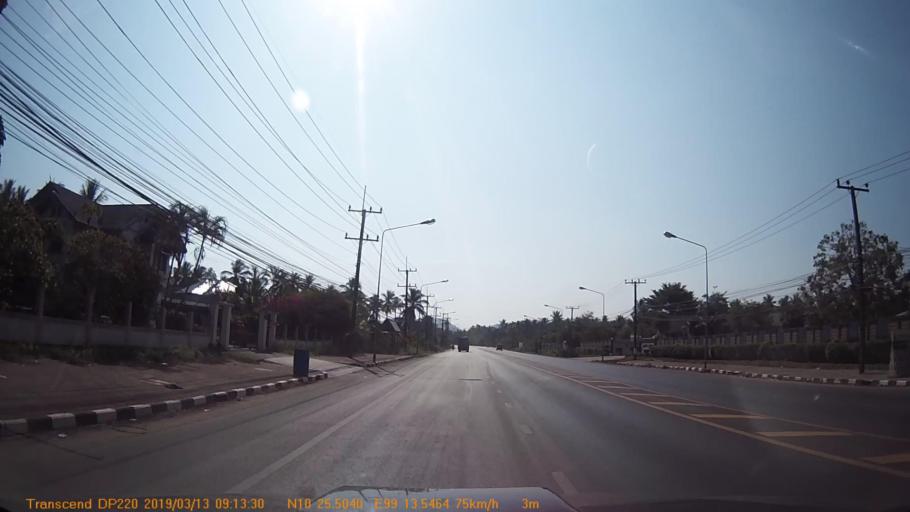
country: TH
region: Chumphon
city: Chumphon
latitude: 10.4249
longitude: 99.2260
